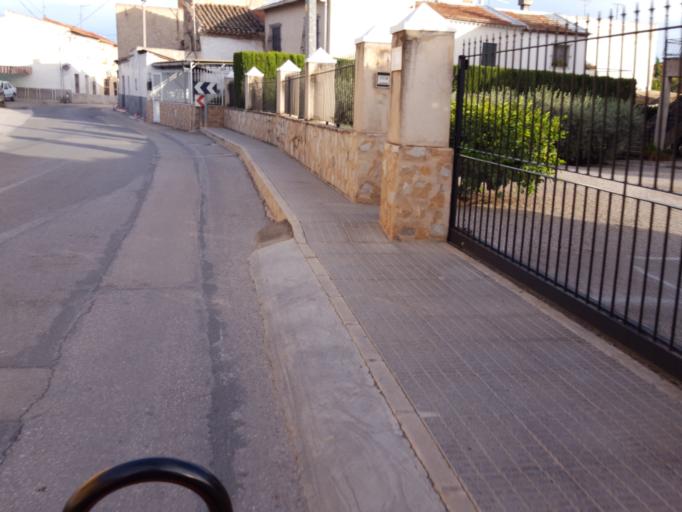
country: ES
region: Murcia
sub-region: Murcia
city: Murcia
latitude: 37.9881
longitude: -1.1581
